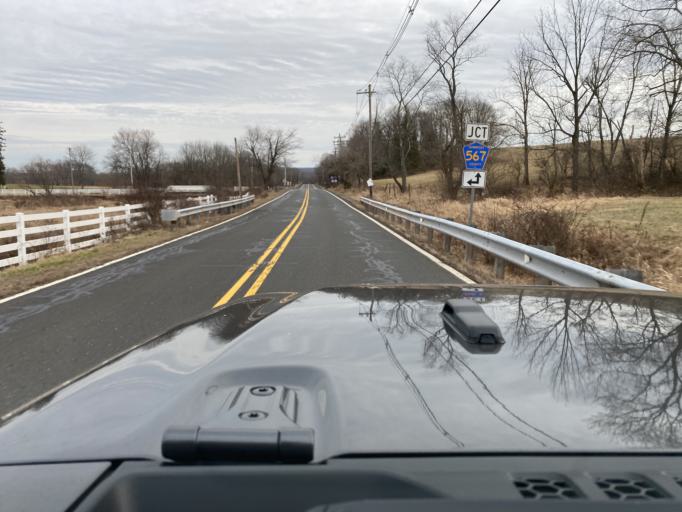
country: US
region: New Jersey
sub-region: Somerset County
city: Bradley Gardens
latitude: 40.5211
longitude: -74.7372
